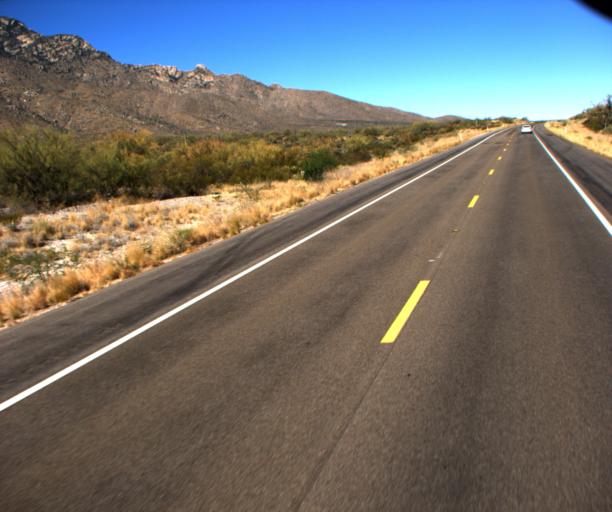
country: US
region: Arizona
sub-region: Pima County
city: Three Points
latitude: 32.0382
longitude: -111.5067
